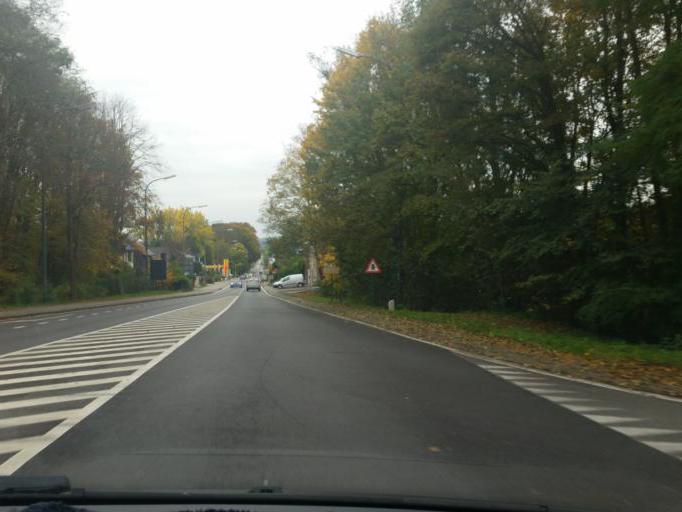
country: BE
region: Flanders
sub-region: Provincie Vlaams-Brabant
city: Beersel
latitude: 50.7411
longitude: 4.2756
